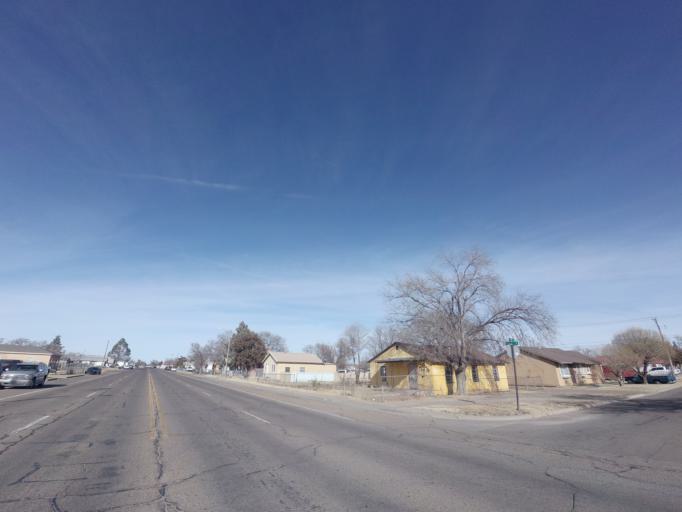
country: US
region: New Mexico
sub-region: Curry County
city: Clovis
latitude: 34.4018
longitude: -103.2205
